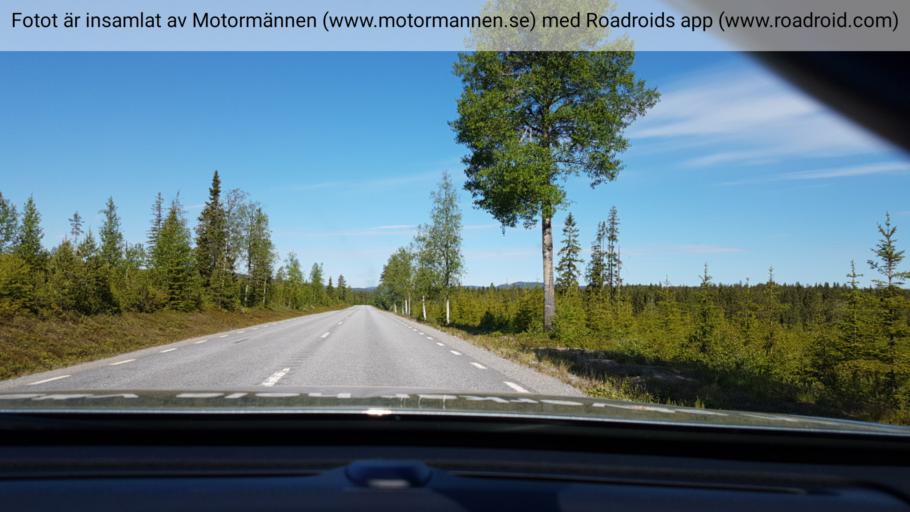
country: SE
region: Vaesterbotten
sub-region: Bjurholms Kommun
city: Bjurholm
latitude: 63.9586
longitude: 18.8654
